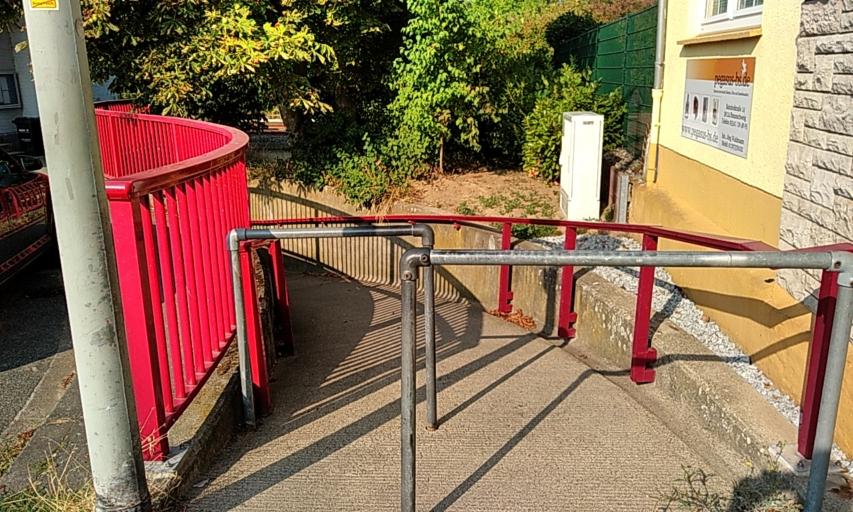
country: DE
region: Lower Saxony
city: Leiferde
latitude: 52.2043
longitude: 10.5043
